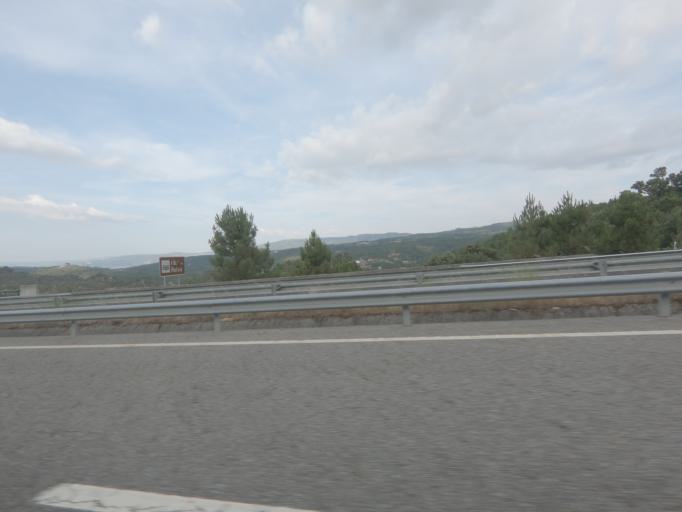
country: PT
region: Vila Real
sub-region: Chaves
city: Chaves
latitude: 41.6991
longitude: -7.5519
